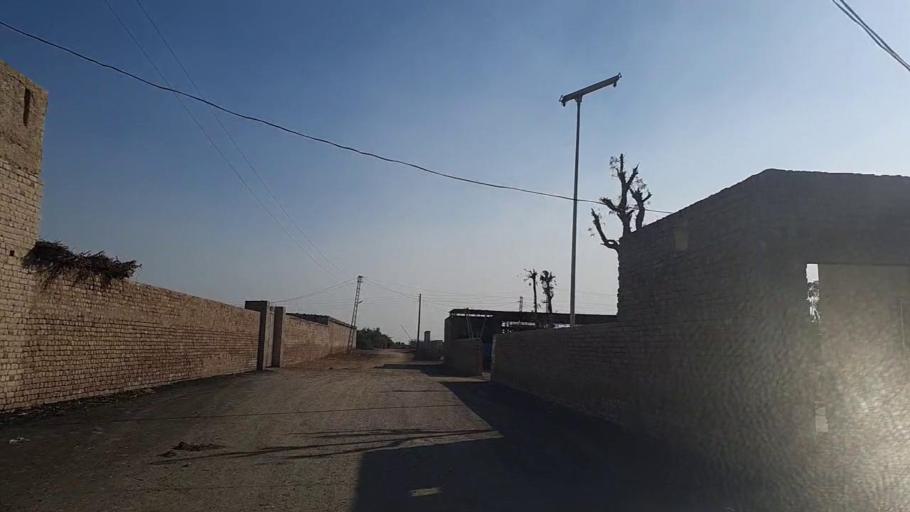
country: PK
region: Sindh
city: Shahpur Chakar
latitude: 26.2160
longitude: 68.6424
